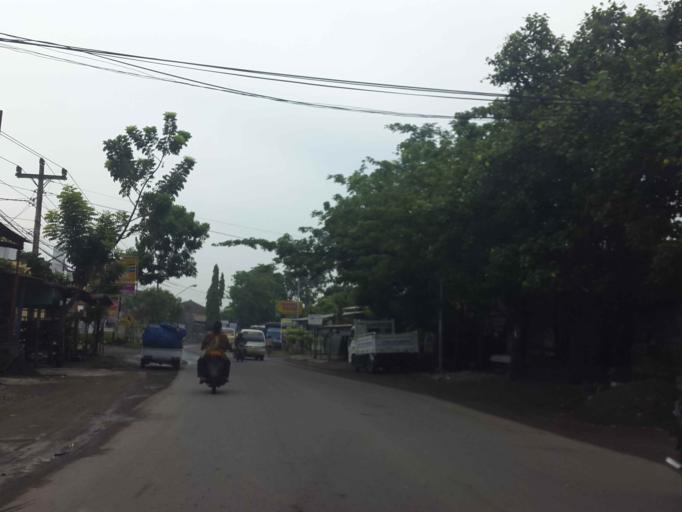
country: ID
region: Central Java
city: Semarang
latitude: -6.9890
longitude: 110.4737
